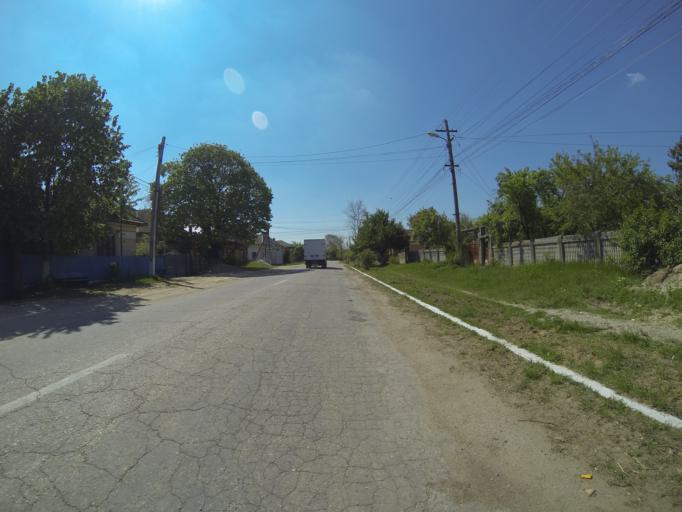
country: RO
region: Dolj
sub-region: Comuna Caraula
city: Caraula
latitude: 44.1953
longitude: 23.2473
